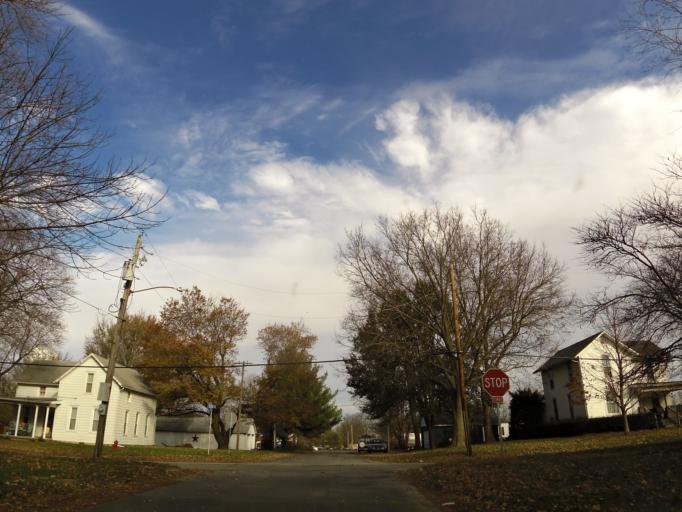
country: US
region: Illinois
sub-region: De Witt County
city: Farmer City
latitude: 40.2447
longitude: -88.6379
